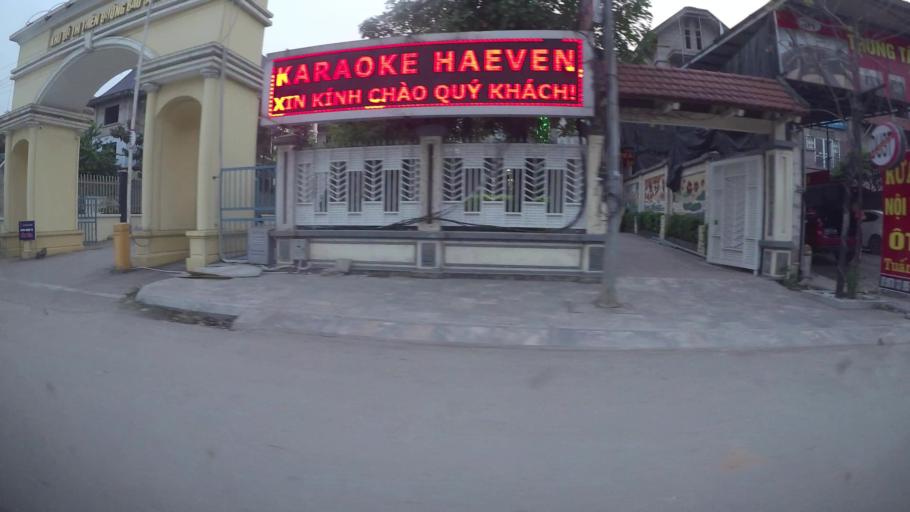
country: VN
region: Ha Noi
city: Cau Dien
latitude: 21.0015
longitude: 105.7330
